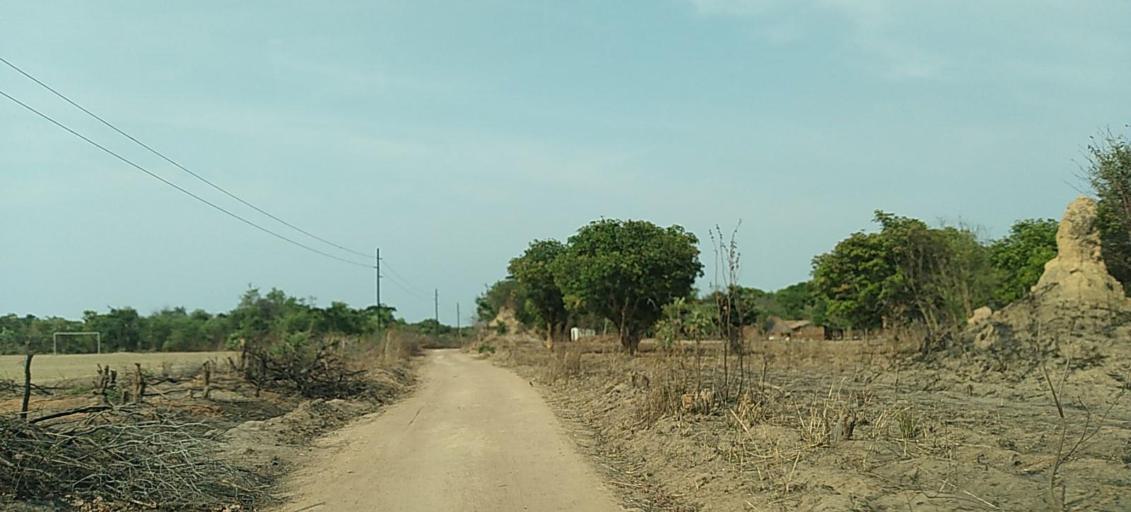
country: ZM
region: Copperbelt
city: Ndola
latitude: -13.2206
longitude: 28.6789
